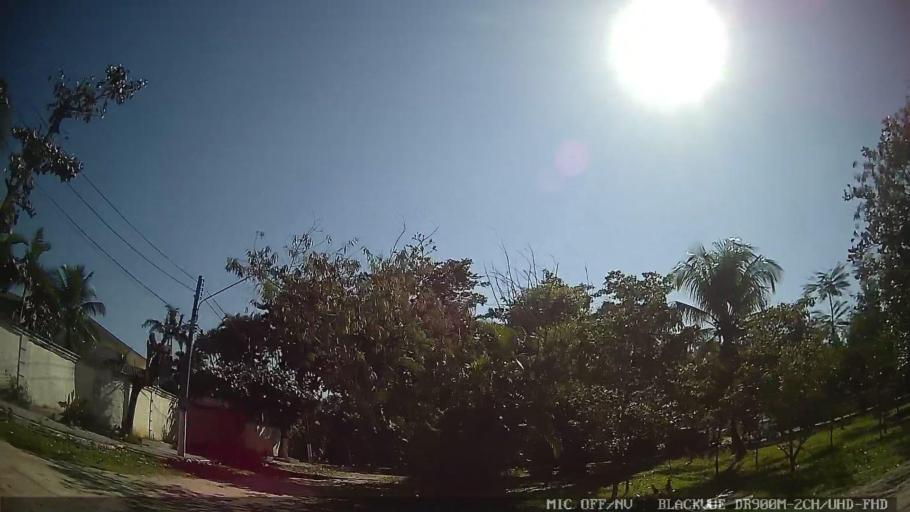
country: BR
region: Sao Paulo
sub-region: Guaruja
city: Guaruja
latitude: -23.9836
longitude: -46.2095
